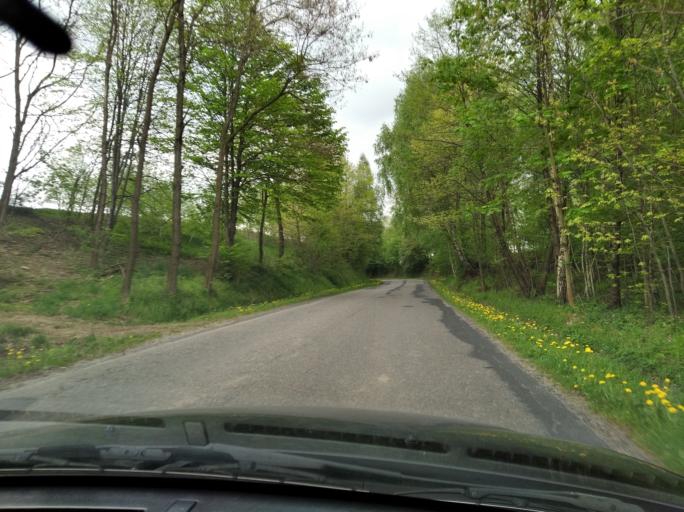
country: PL
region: Lesser Poland Voivodeship
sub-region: Powiat tarnowski
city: Szynwald
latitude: 49.9872
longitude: 21.1208
